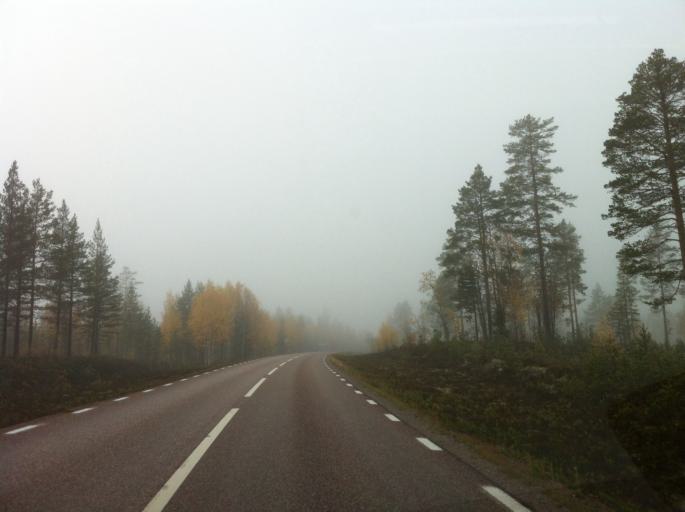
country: NO
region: Hedmark
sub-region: Trysil
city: Innbygda
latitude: 61.6923
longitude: 13.0683
